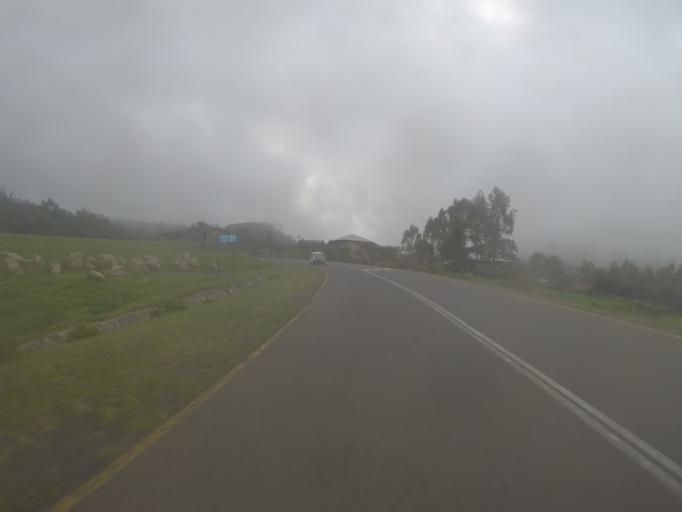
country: ET
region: Amhara
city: Gondar
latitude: 12.7362
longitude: 37.5164
